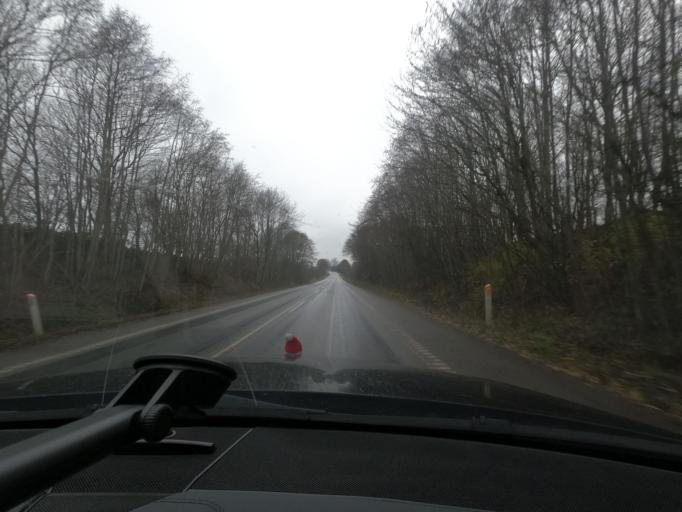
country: DK
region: South Denmark
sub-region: Sonderborg Kommune
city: Horuphav
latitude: 54.8968
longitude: 9.9630
